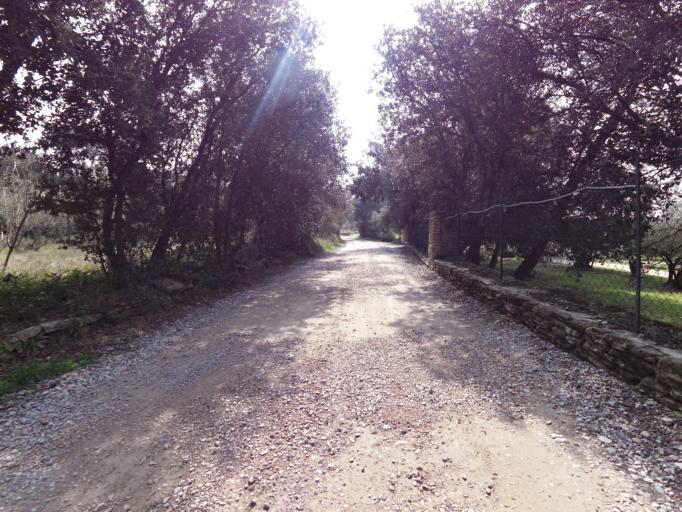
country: FR
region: Languedoc-Roussillon
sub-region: Departement du Gard
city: Aubais
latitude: 43.7487
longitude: 4.1586
